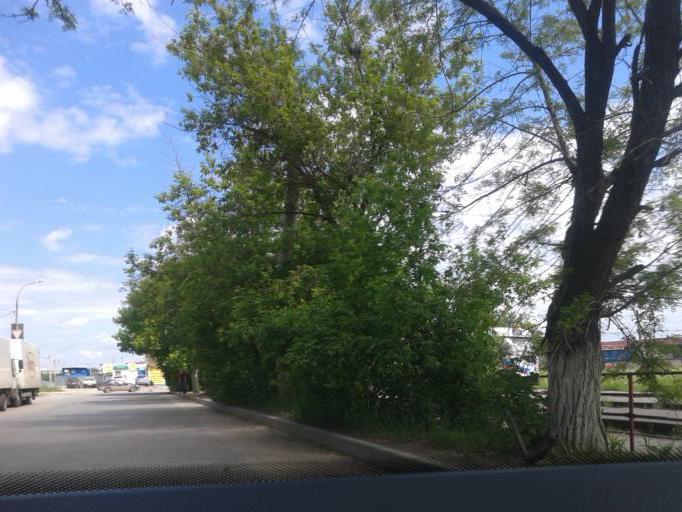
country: RU
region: Volgograd
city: Gorodishche
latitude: 48.7710
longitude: 44.5041
